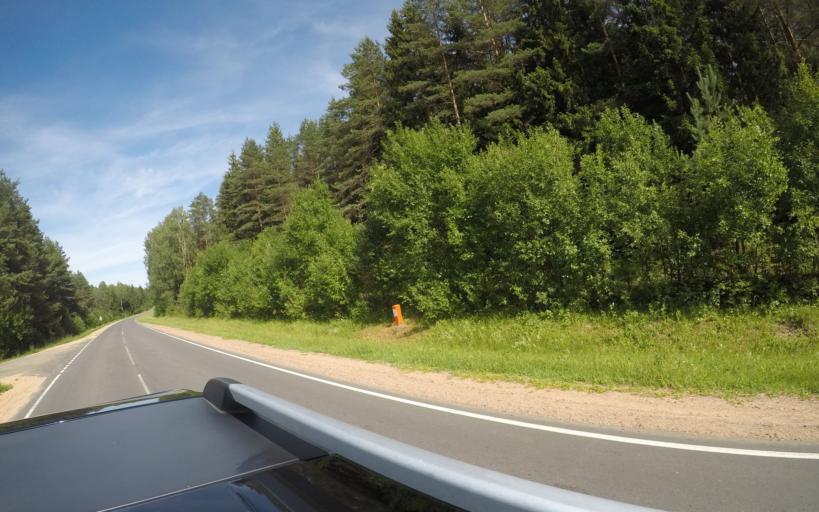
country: BY
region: Grodnenskaya
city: Hal'shany
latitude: 54.2746
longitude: 26.0357
